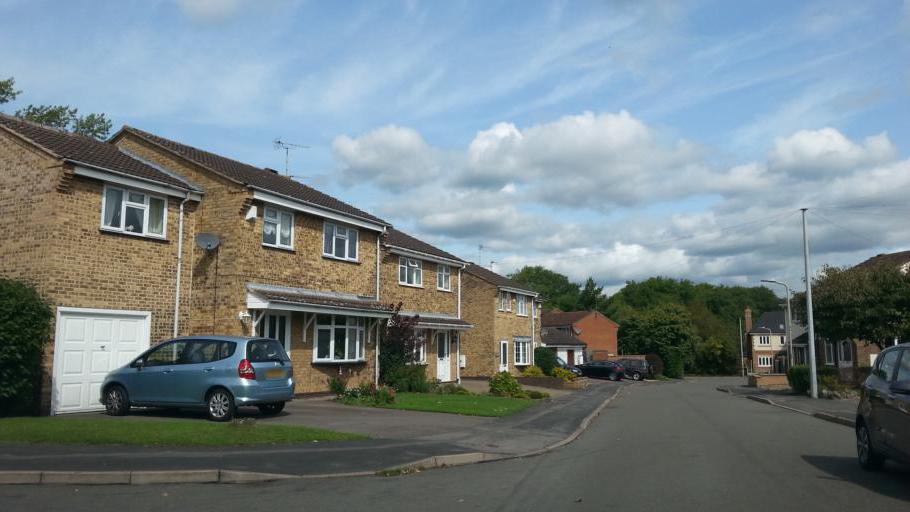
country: GB
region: England
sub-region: Leicestershire
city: Blaby
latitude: 52.5731
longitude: -1.1815
